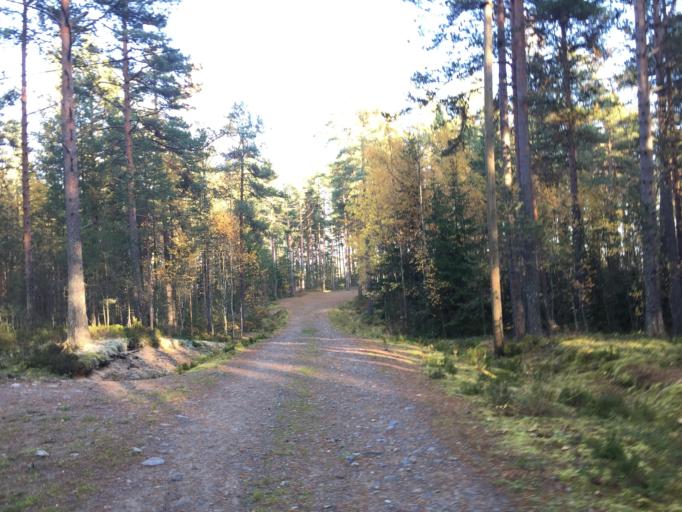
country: RU
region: Republic of Karelia
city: Lakhdenpokh'ya
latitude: 61.2858
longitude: 30.1329
